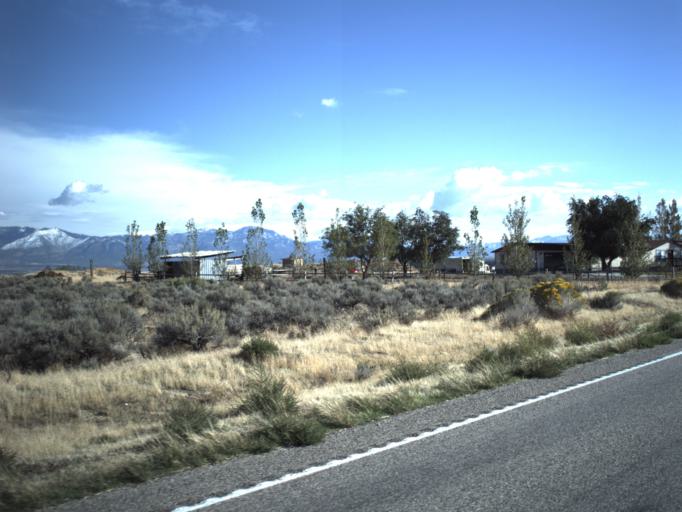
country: US
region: Utah
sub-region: Millard County
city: Fillmore
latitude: 39.1771
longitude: -112.4101
